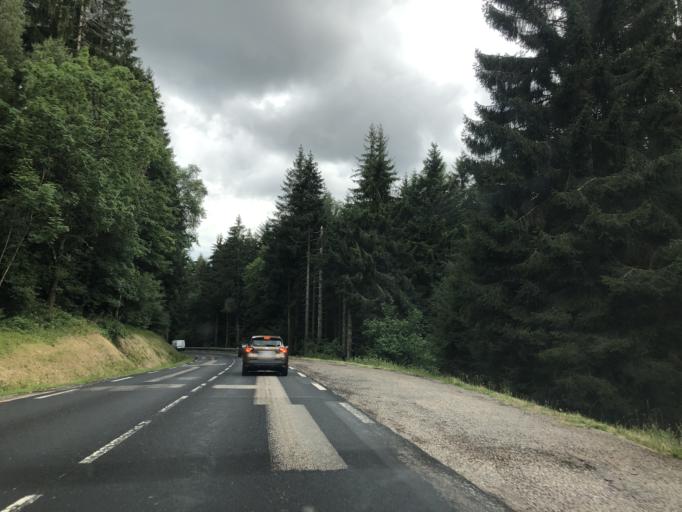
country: FR
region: Lorraine
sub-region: Departement des Vosges
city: Xonrupt-Longemer
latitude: 48.0946
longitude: 6.9019
